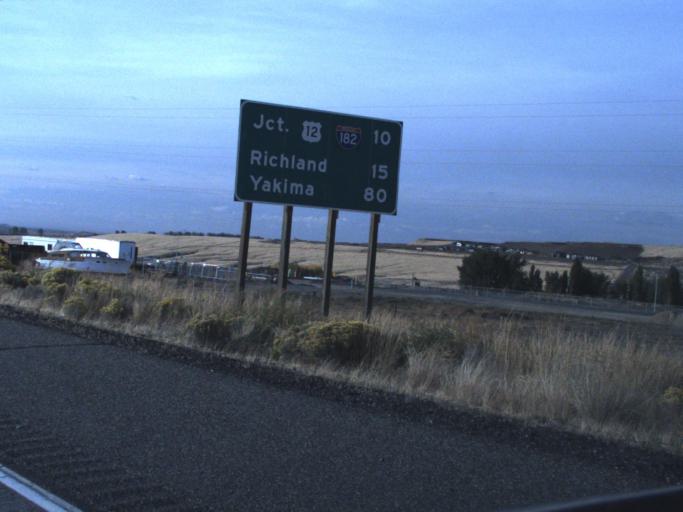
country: US
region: Washington
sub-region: Franklin County
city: West Pasco
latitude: 46.1727
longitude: -119.2102
